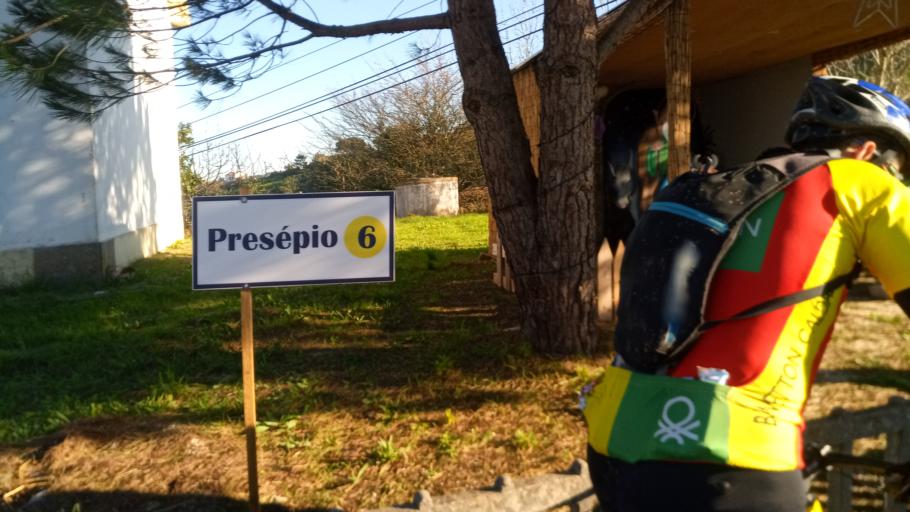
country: PT
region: Leiria
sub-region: Caldas da Rainha
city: Caldas da Rainha
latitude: 39.3590
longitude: -9.0512
